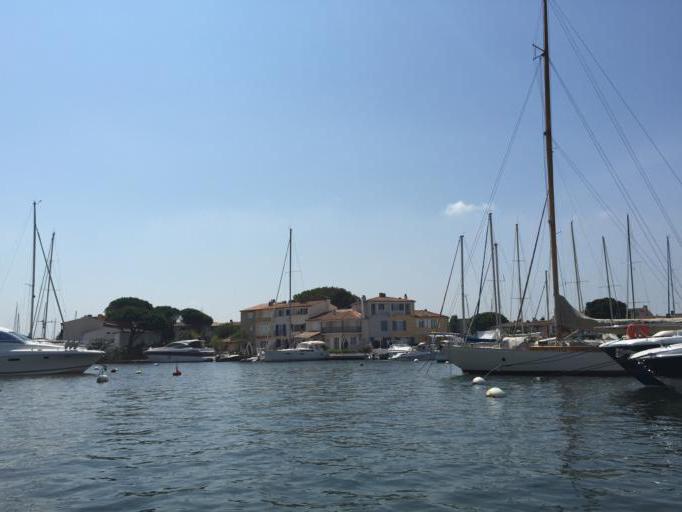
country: FR
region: Provence-Alpes-Cote d'Azur
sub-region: Departement du Var
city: Gassin
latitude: 43.2727
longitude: 6.5800
